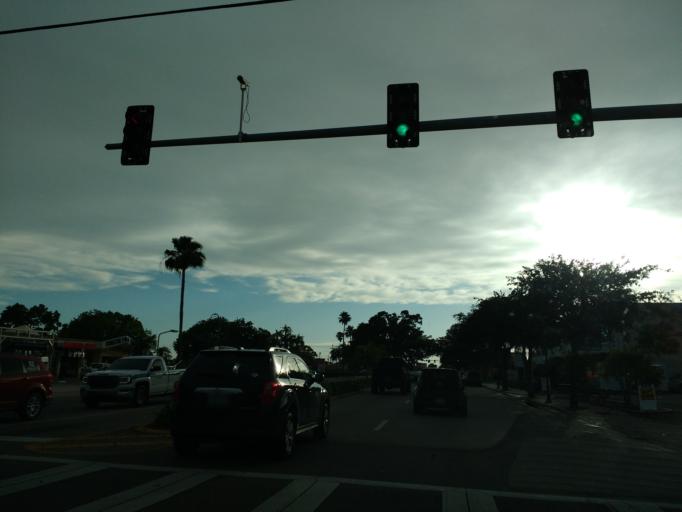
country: US
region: Florida
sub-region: Lee County
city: Cape Coral
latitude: 26.5627
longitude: -81.9502
